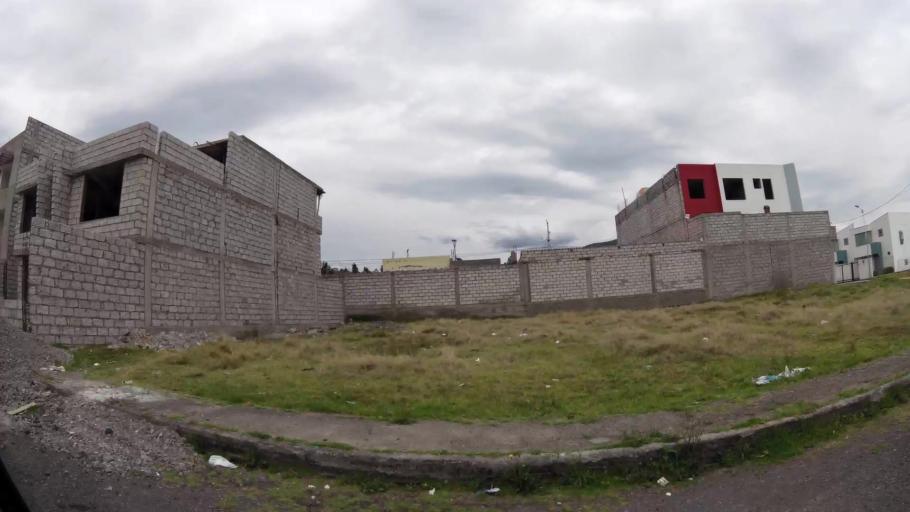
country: EC
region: Cotopaxi
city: Latacunga
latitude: -0.9687
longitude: -78.6113
